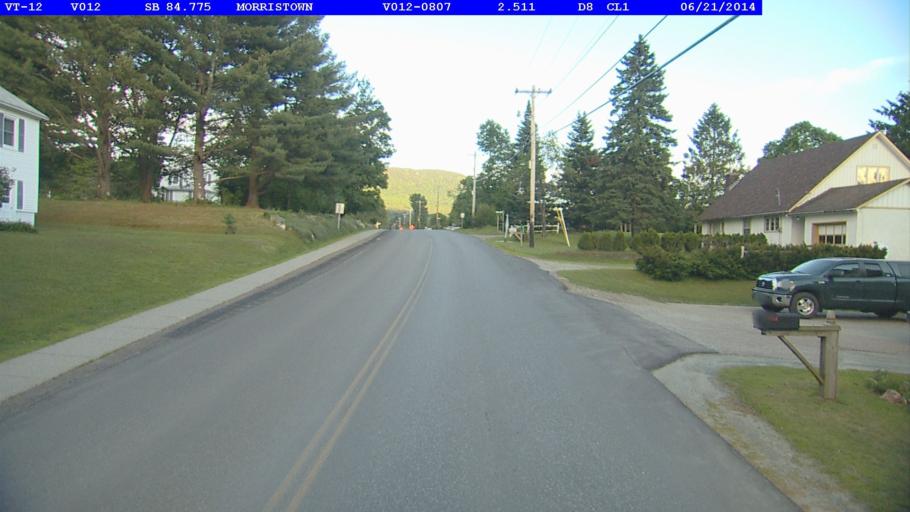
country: US
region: Vermont
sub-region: Lamoille County
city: Morrisville
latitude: 44.5569
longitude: -72.5831
